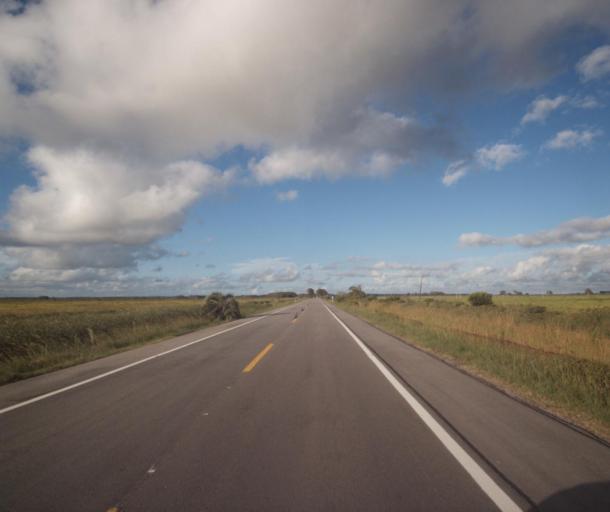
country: BR
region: Rio Grande do Sul
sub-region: Rio Grande
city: Rio Grande
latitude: -32.1422
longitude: -52.3823
